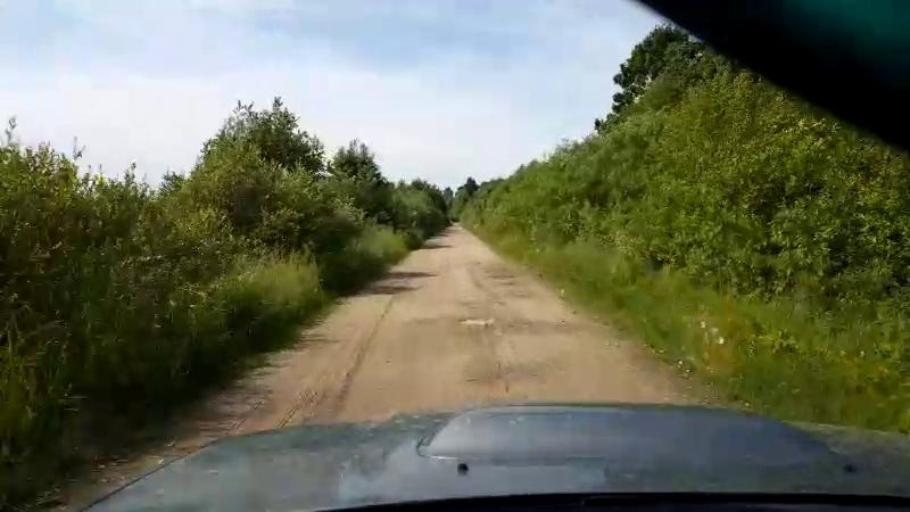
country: EE
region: Paernumaa
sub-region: Tootsi vald
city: Tootsi
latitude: 58.5241
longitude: 24.7047
